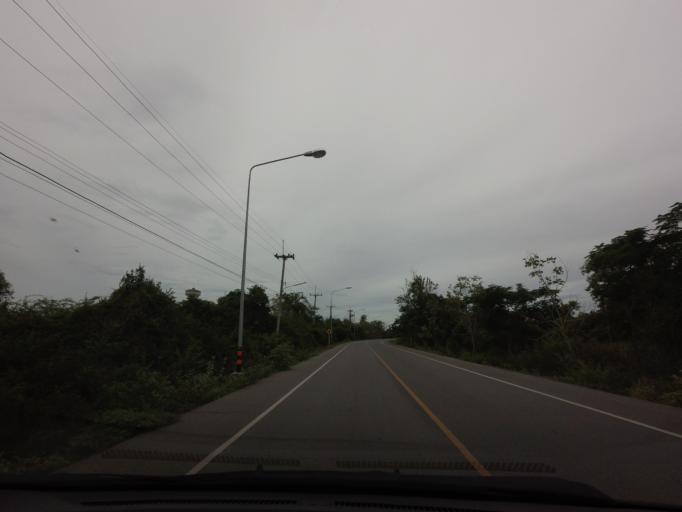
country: TH
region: Phetchaburi
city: Cha-am
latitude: 12.8433
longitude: 99.9915
